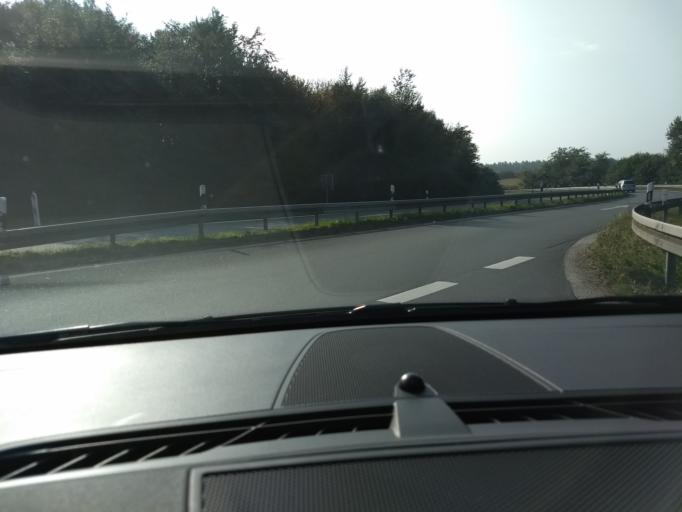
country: DE
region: North Rhine-Westphalia
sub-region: Regierungsbezirk Munster
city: Heiden
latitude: 51.8080
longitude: 6.9819
